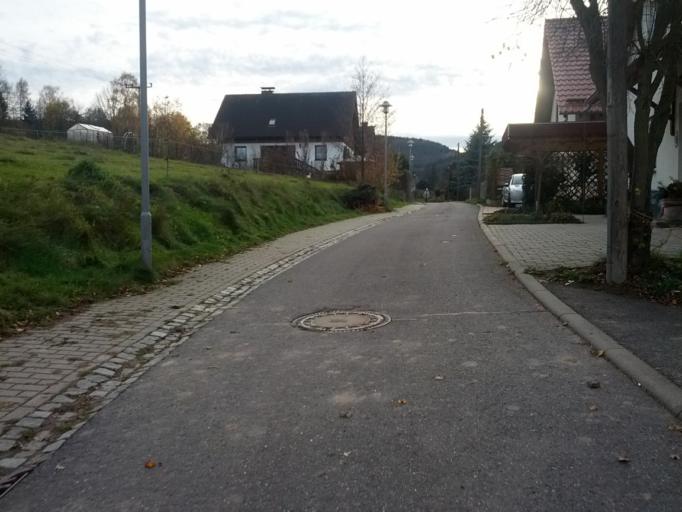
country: DE
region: Thuringia
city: Thal
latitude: 50.9321
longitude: 10.3567
